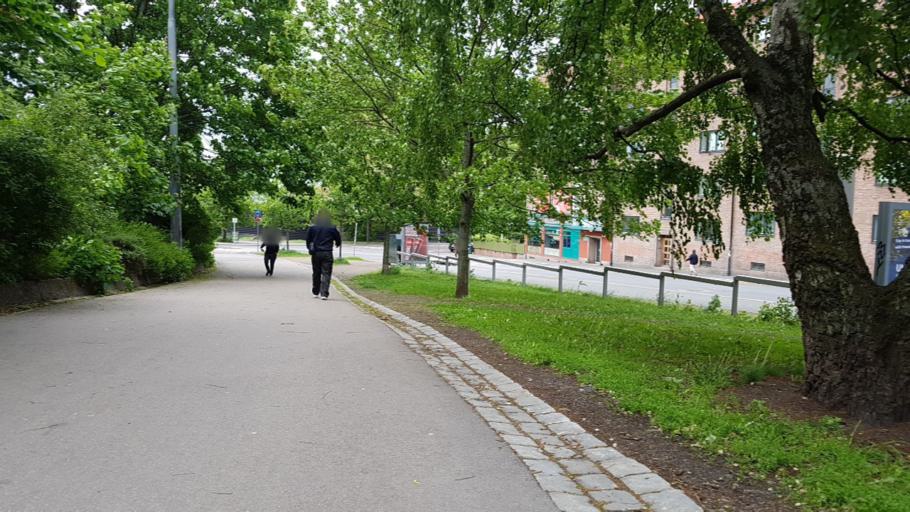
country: NO
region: Oslo
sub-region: Oslo
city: Oslo
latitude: 59.9277
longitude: 10.7666
